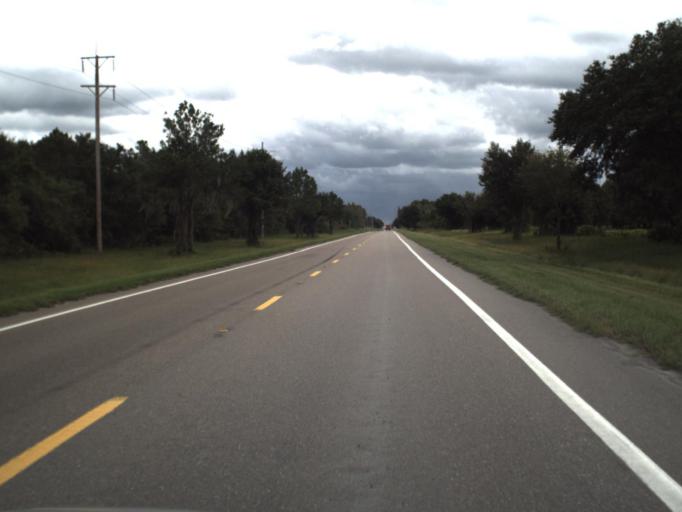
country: US
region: Florida
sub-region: Hardee County
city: Bowling Green
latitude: 27.6506
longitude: -82.0520
